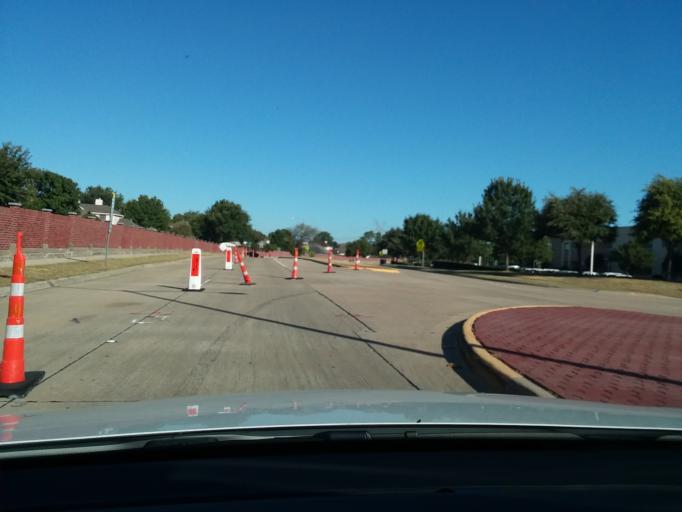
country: US
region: Texas
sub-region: Denton County
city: Lewisville
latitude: 33.0597
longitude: -97.0193
